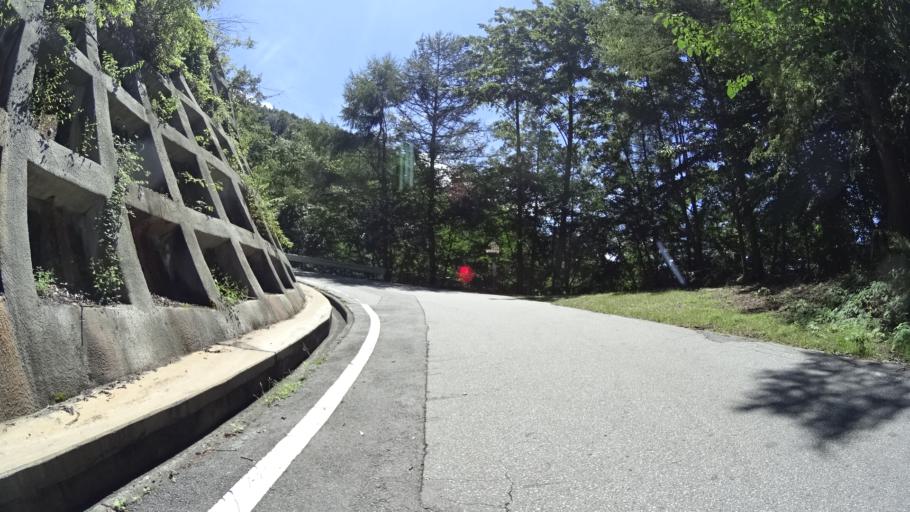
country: JP
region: Yamanashi
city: Enzan
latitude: 35.7424
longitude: 138.8286
